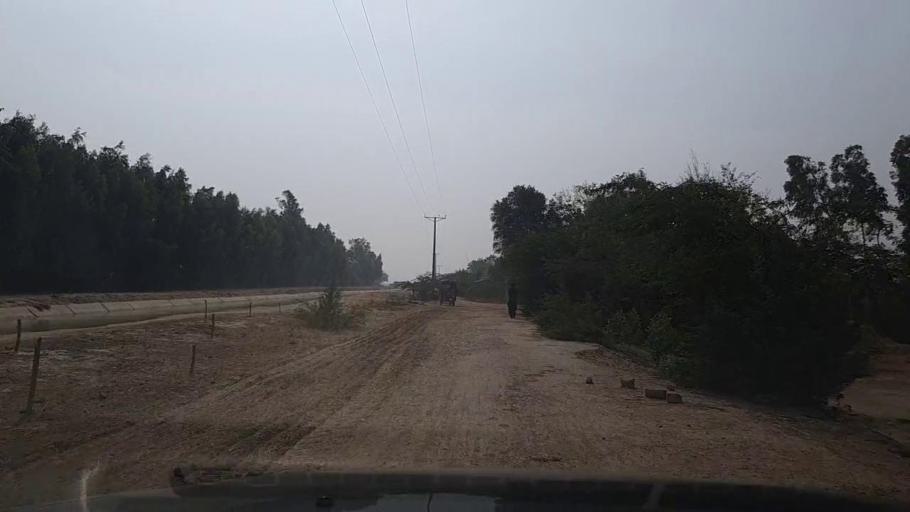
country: PK
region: Sindh
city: Mirpur Sakro
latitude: 24.5365
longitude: 67.8120
